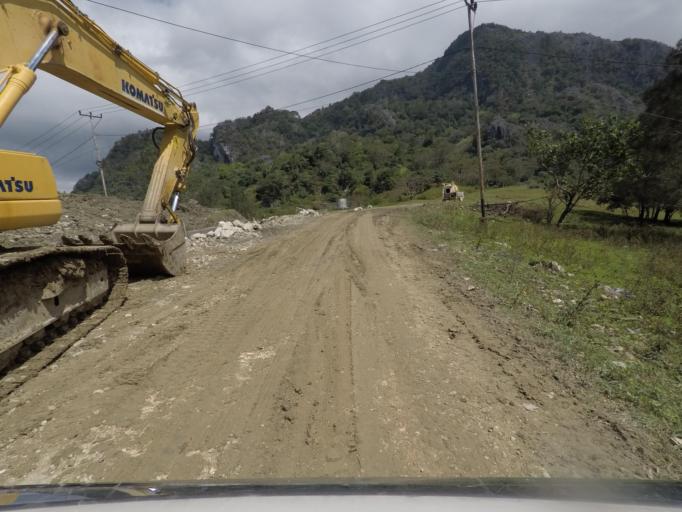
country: TL
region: Baucau
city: Venilale
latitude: -8.7265
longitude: 126.3687
